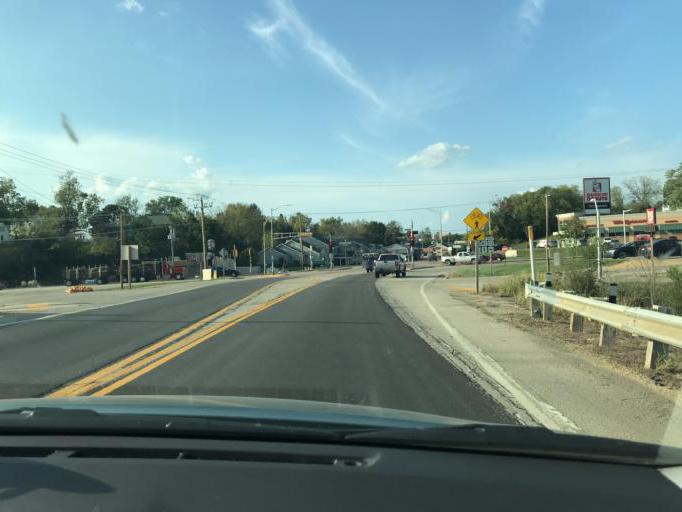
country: US
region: Wisconsin
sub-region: Grant County
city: Platteville
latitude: 42.7263
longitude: -90.4757
